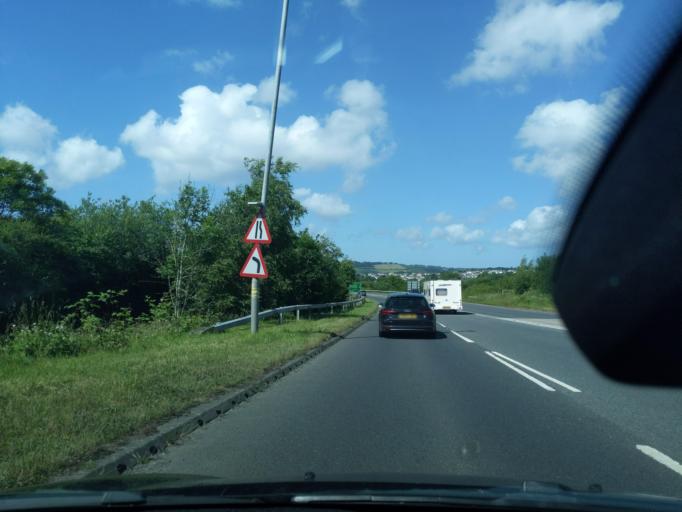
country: GB
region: England
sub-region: Devon
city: Barnstaple
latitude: 51.0650
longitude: -4.0594
